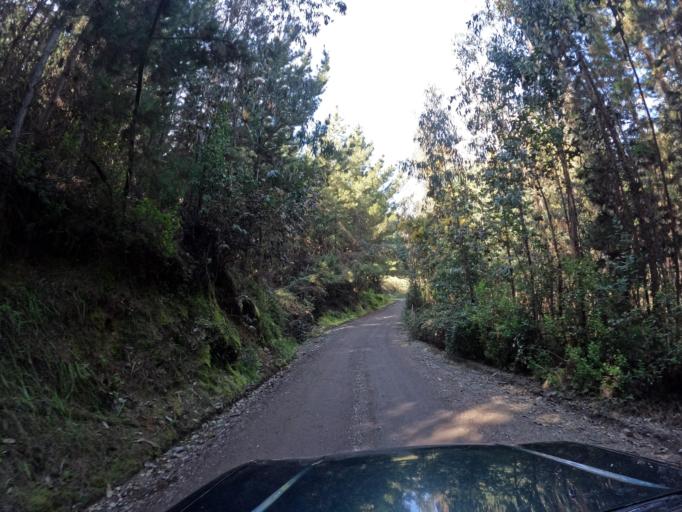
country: CL
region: Biobio
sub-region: Provincia de Concepcion
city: Chiguayante
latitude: -37.0615
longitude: -72.8911
